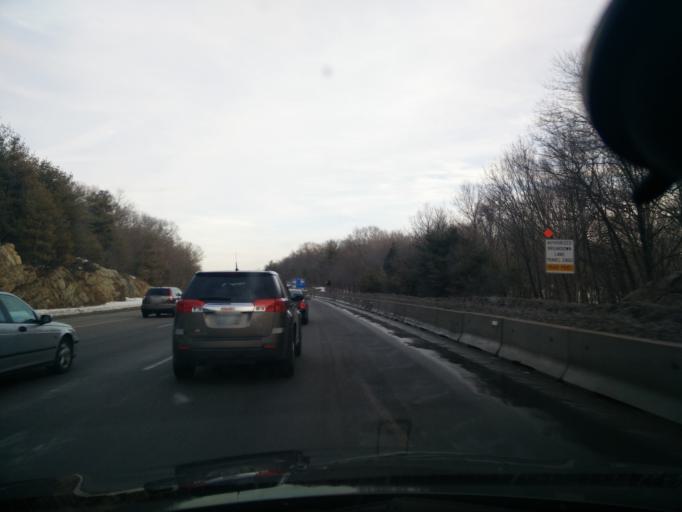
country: US
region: Massachusetts
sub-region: Norfolk County
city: Westwood
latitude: 42.2391
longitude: -71.2015
